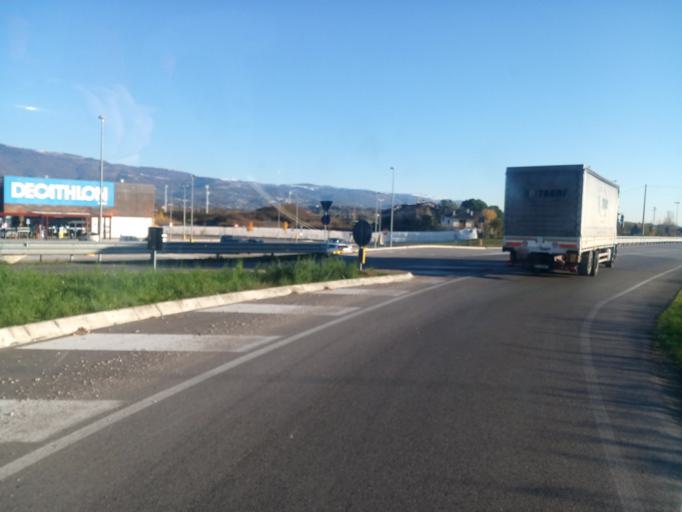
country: IT
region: Veneto
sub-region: Provincia di Vicenza
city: Thiene
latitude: 45.6941
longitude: 11.4969
